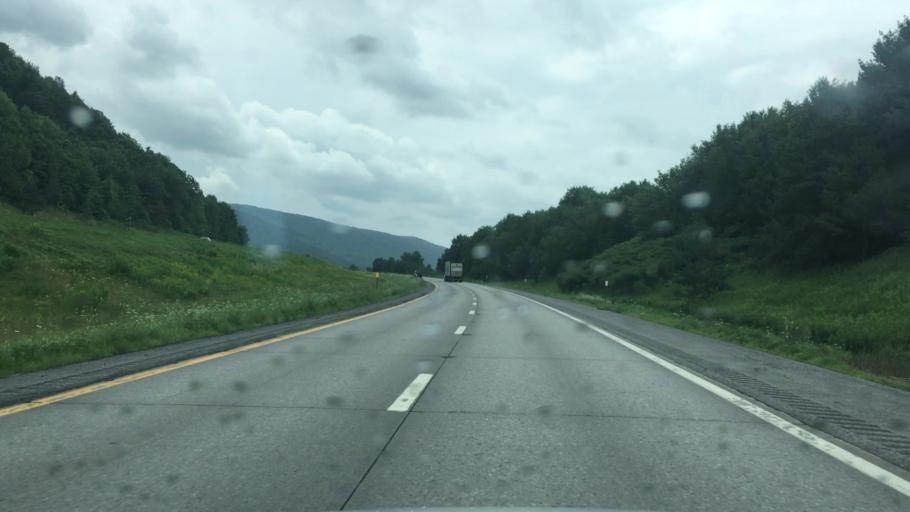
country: US
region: New York
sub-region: Otsego County
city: Worcester
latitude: 42.5824
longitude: -74.7621
